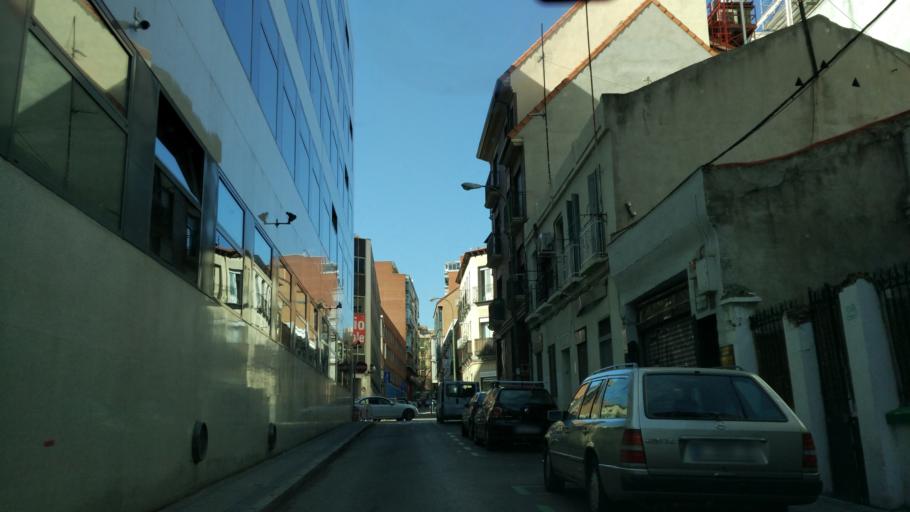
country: ES
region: Madrid
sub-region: Provincia de Madrid
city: Tetuan de las Victorias
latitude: 40.4546
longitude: -3.6999
